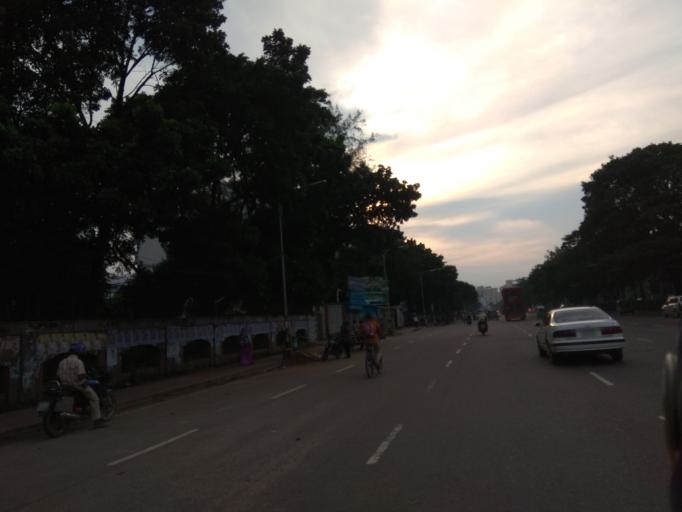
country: BD
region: Dhaka
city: Azimpur
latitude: 23.7584
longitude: 90.3799
